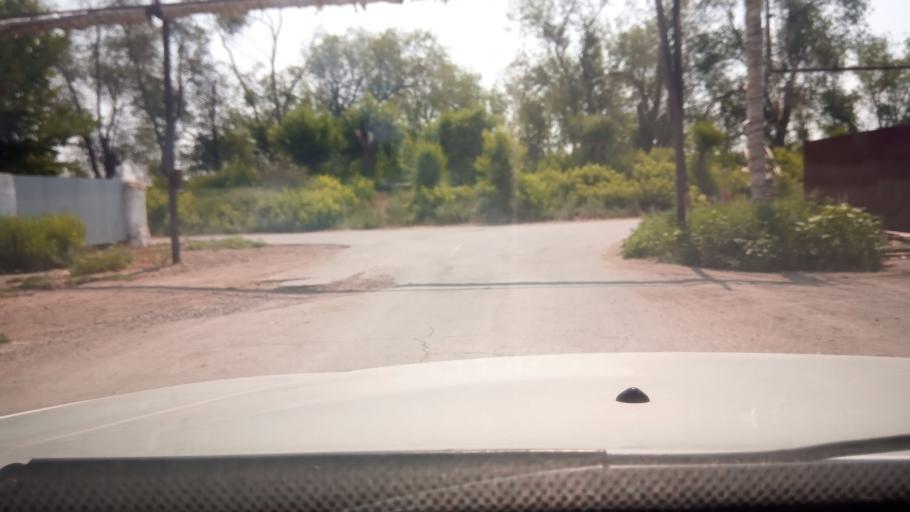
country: RU
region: Orenburg
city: Novotroitsk
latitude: 51.1950
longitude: 58.3332
